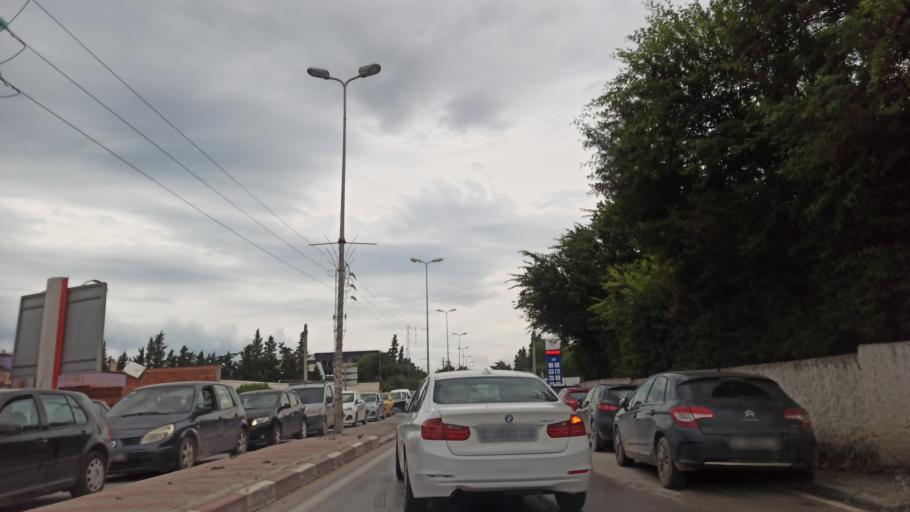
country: TN
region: Ariana
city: Ariana
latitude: 36.8746
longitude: 10.2459
